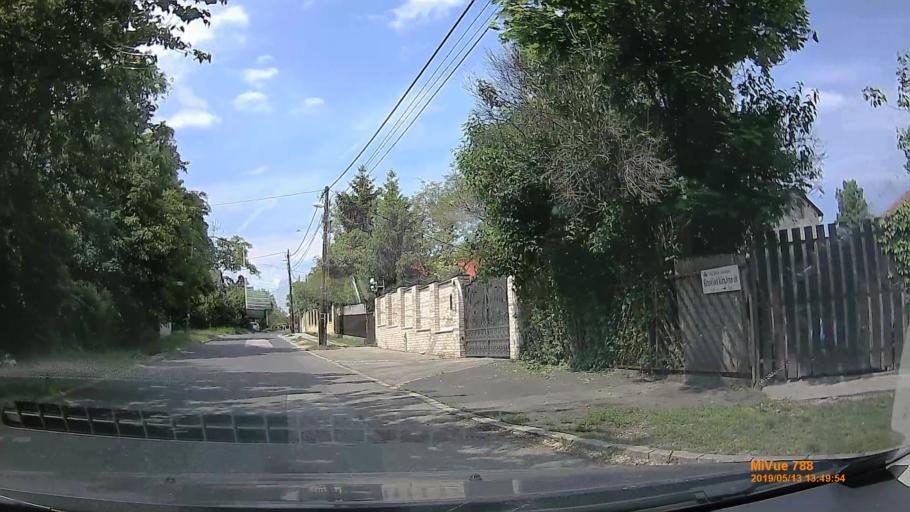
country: HU
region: Budapest
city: Budapest XXII. keruelet
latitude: 47.4202
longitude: 19.0120
